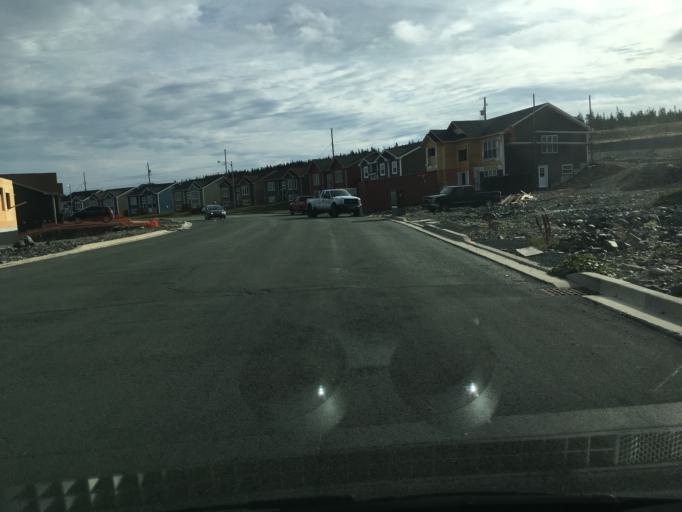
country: CA
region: Newfoundland and Labrador
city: Mount Pearl
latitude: 47.5575
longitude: -52.8035
